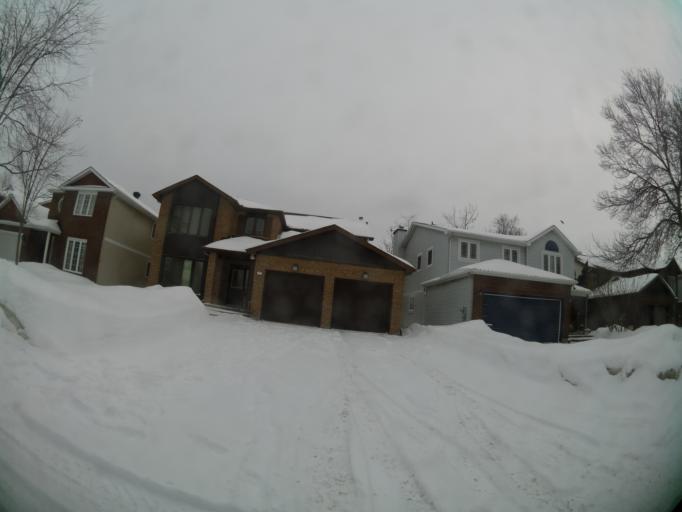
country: CA
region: Ontario
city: Ottawa
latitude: 45.3707
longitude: -75.6162
